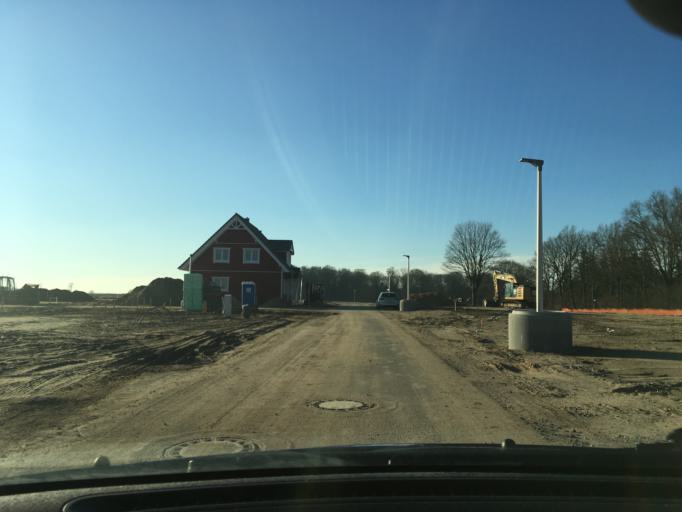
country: DE
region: Schleswig-Holstein
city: Buchen
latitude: 53.4776
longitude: 10.5978
